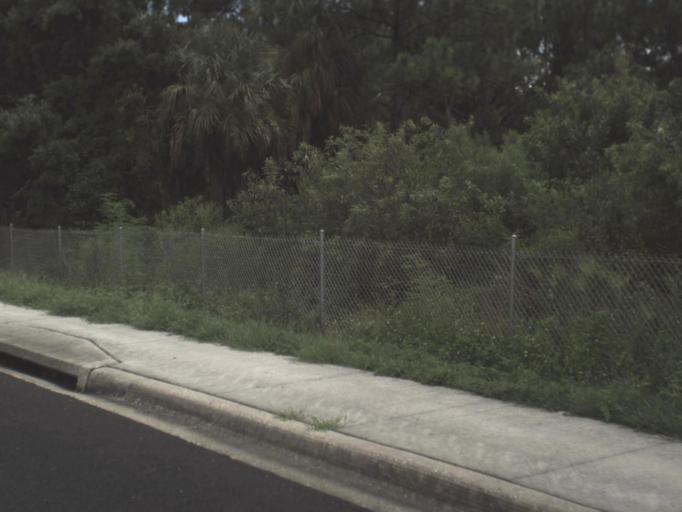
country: US
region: Florida
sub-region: Hillsborough County
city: Westchase
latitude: 28.0231
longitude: -82.6282
